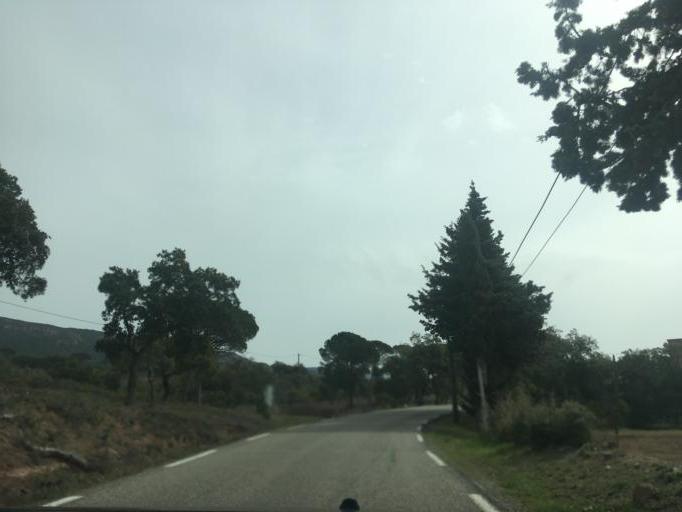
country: FR
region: Provence-Alpes-Cote d'Azur
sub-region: Departement du Var
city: Le Muy
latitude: 43.5099
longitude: 6.6104
